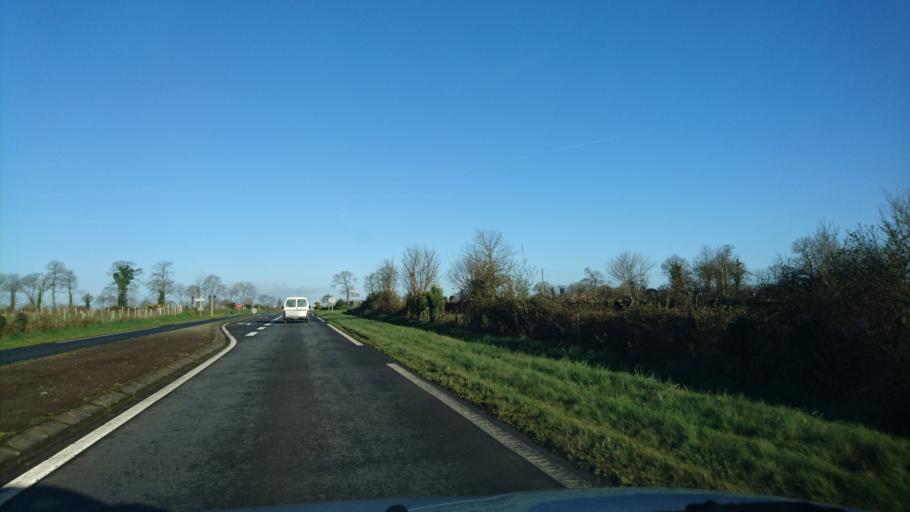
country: FR
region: Brittany
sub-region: Departement d'Ille-et-Vilaine
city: La Boussac
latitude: 48.5036
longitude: -1.6352
